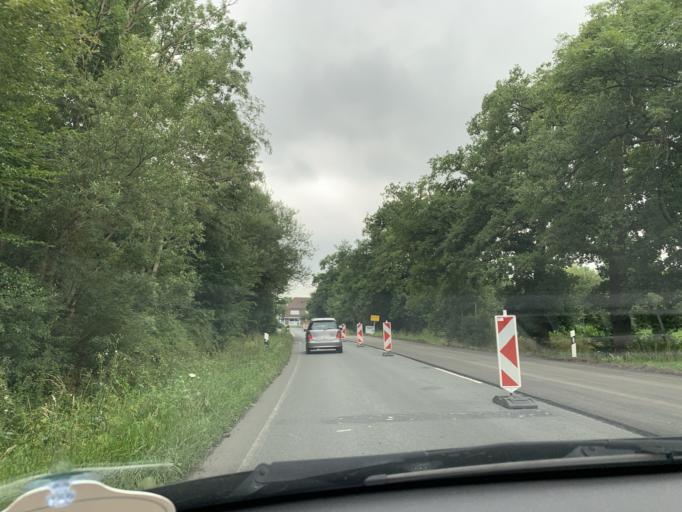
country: DE
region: North Rhine-Westphalia
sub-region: Regierungsbezirk Munster
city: Ennigerloh
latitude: 51.8883
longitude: 8.0442
